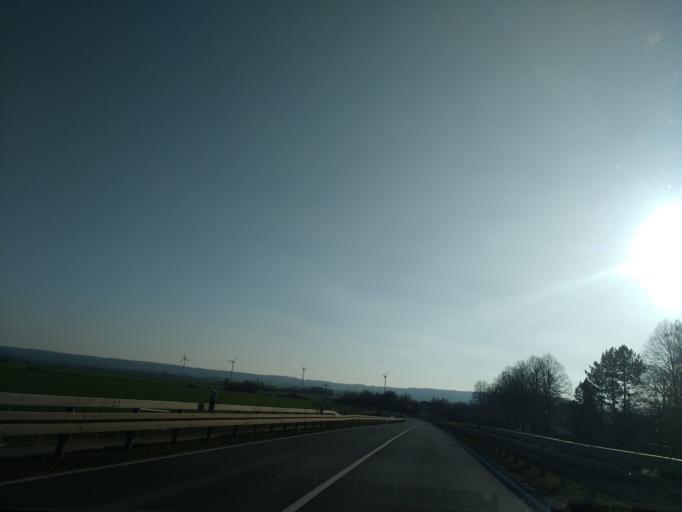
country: DE
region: Lower Saxony
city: Hessisch Oldendorf
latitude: 52.1573
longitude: 9.2490
